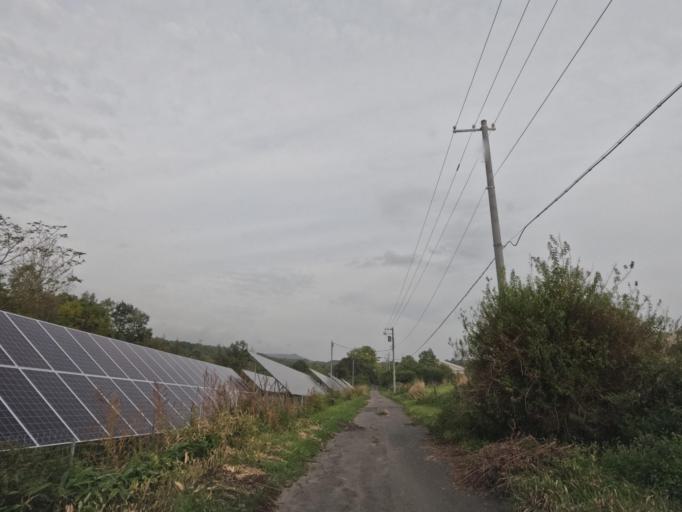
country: JP
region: Hokkaido
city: Date
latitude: 42.4119
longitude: 140.9286
